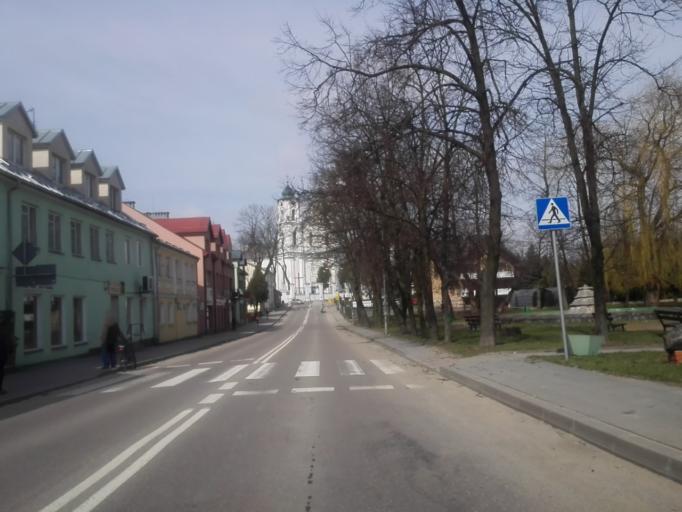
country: PL
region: Podlasie
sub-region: Powiat sejnenski
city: Sejny
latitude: 54.1074
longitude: 23.3480
